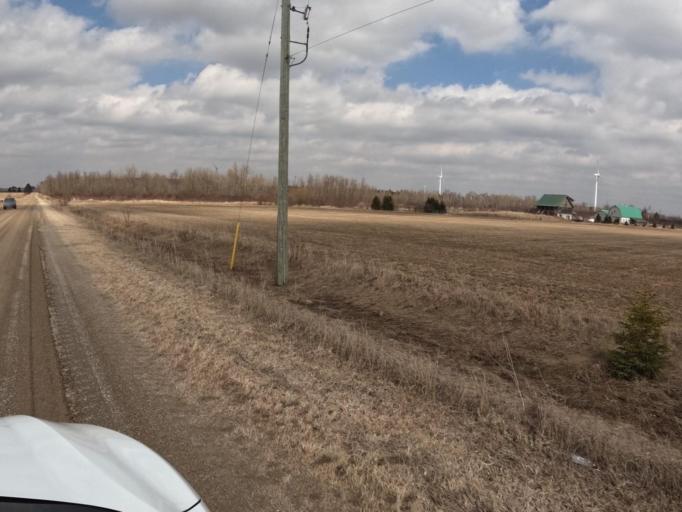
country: CA
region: Ontario
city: Shelburne
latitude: 44.0218
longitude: -80.3299
